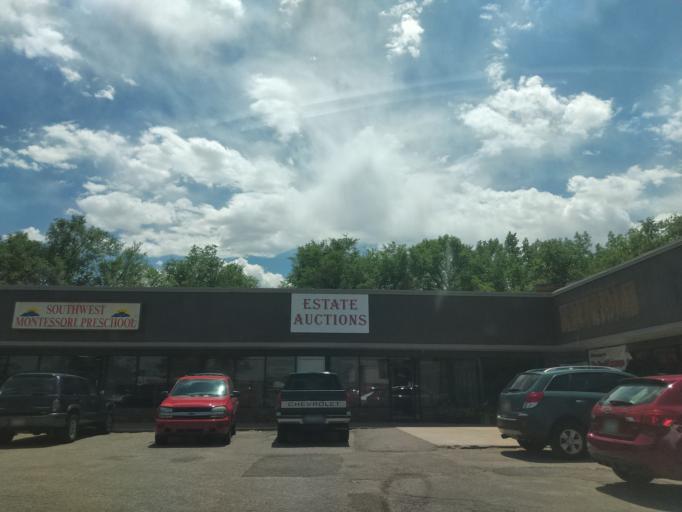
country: US
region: Colorado
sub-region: Jefferson County
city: Lakewood
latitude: 39.6813
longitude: -105.0856
